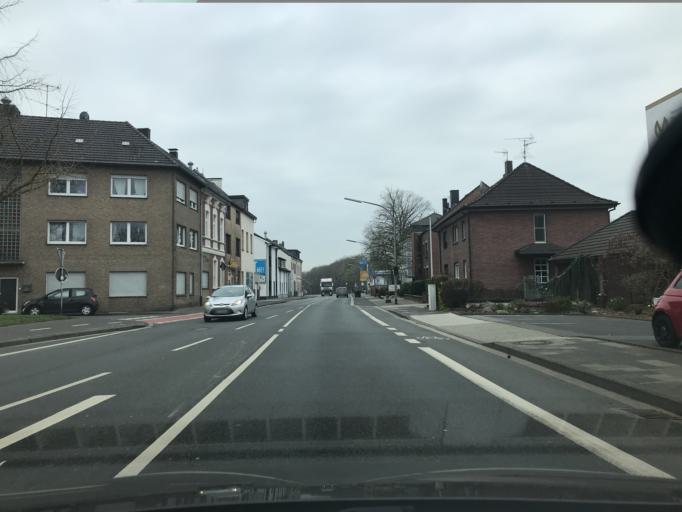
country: DE
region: North Rhine-Westphalia
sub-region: Regierungsbezirk Dusseldorf
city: Viersen
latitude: 51.2620
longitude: 6.3368
